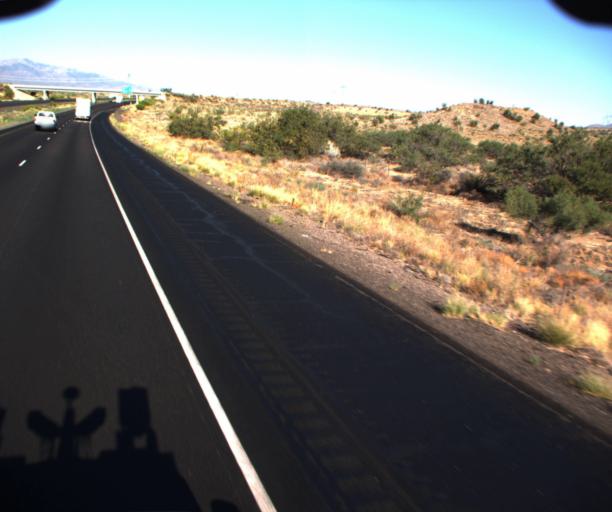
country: US
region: Arizona
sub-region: Mohave County
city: New Kingman-Butler
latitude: 35.1596
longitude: -113.6924
